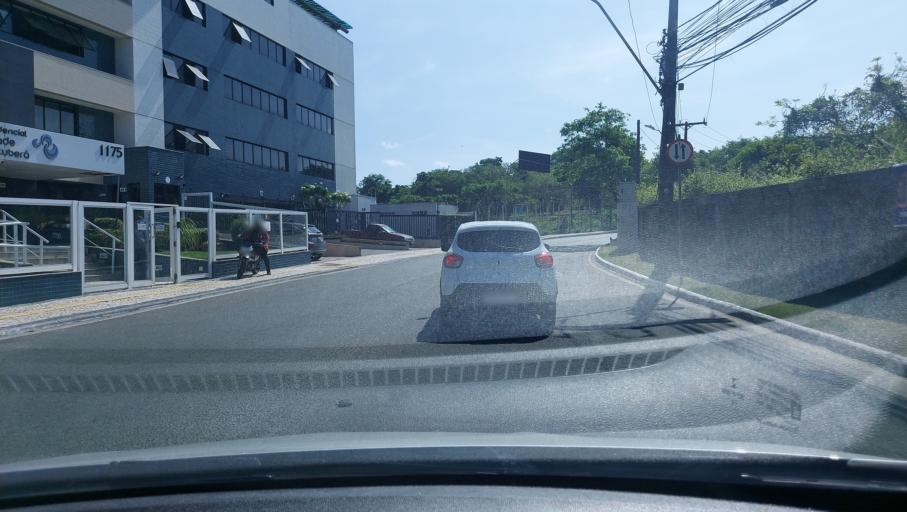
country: BR
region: Bahia
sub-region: Salvador
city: Salvador
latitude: -12.9781
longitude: -38.4425
